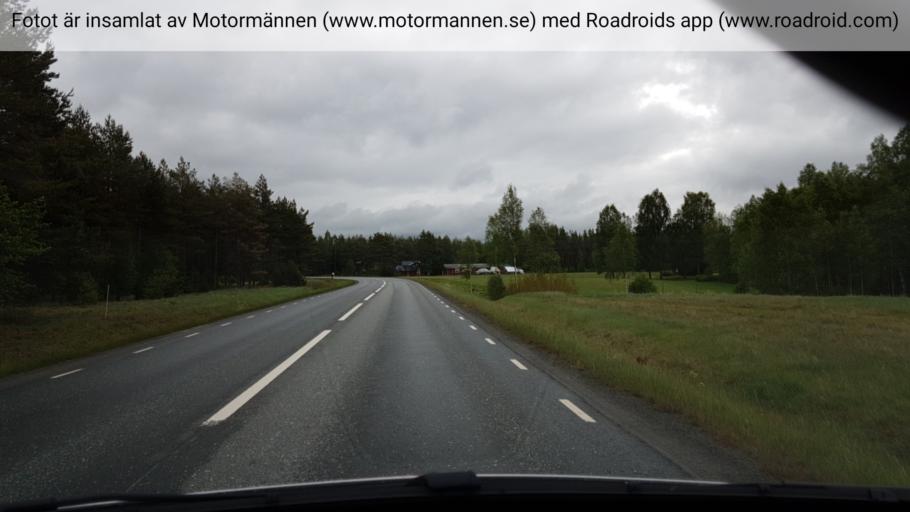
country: SE
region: Joenkoeping
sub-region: Aneby Kommun
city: Aneby
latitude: 57.8164
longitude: 14.7477
